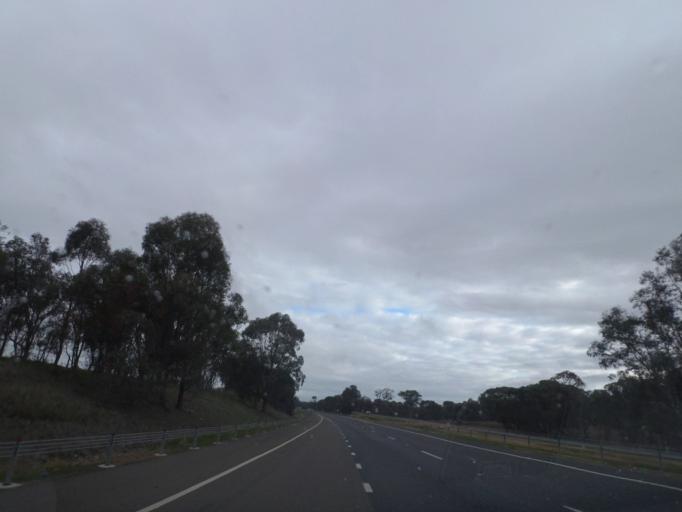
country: AU
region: Victoria
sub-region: Wangaratta
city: Wangaratta
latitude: -36.2250
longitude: 146.4437
